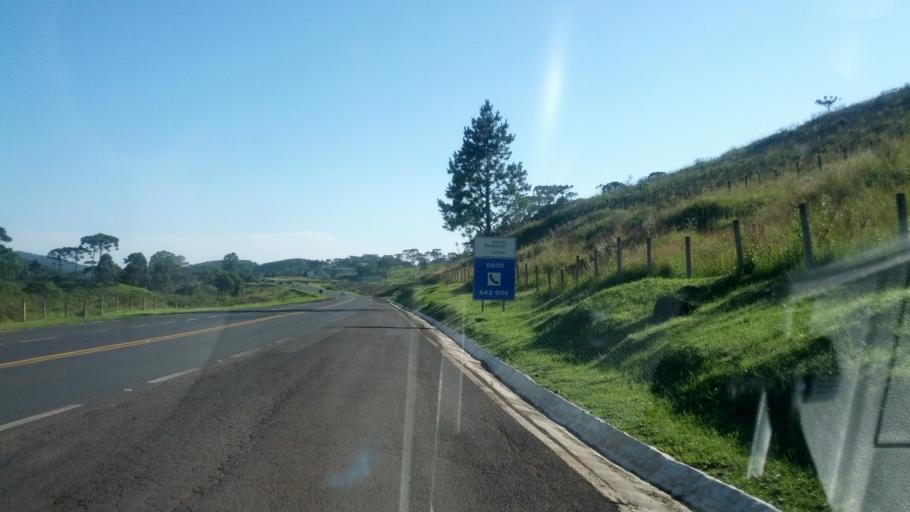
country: BR
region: Santa Catarina
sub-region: Lages
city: Lages
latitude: -27.9561
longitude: -50.4837
